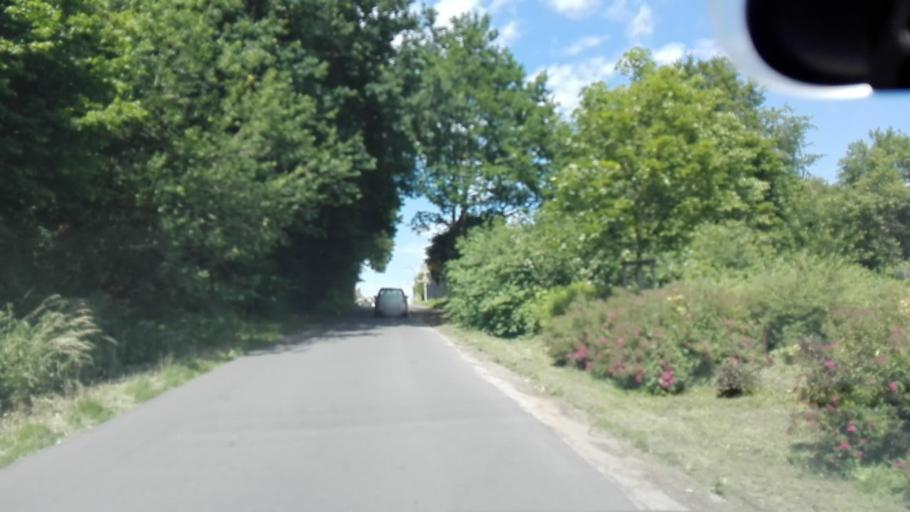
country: DE
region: North Rhine-Westphalia
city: Witten
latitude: 51.4742
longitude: 7.4069
